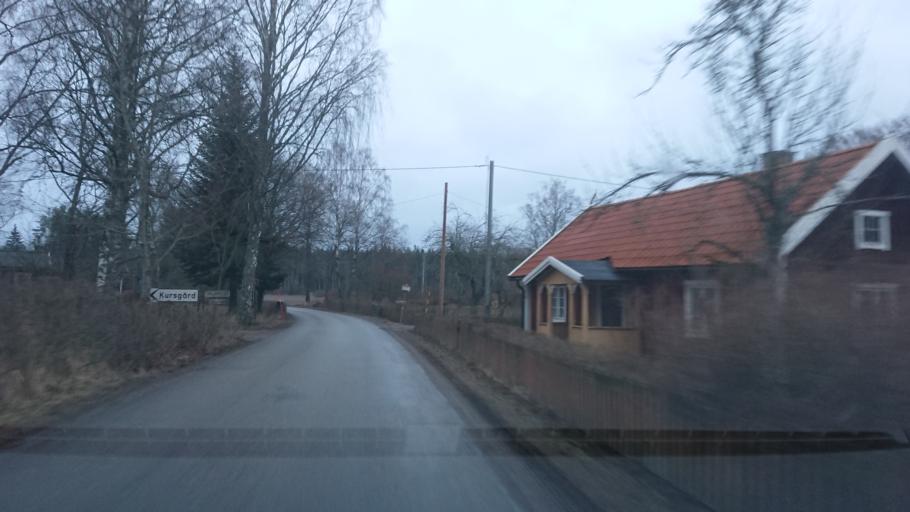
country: SE
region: Uppsala
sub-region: Osthammars Kommun
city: Bjorklinge
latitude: 60.0203
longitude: 17.5849
